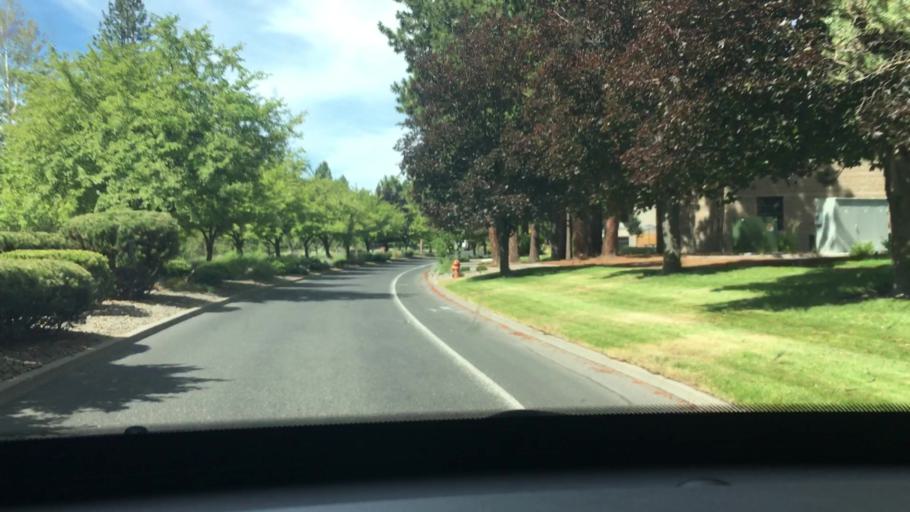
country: US
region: Oregon
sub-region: Deschutes County
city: Bend
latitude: 44.0427
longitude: -121.3281
